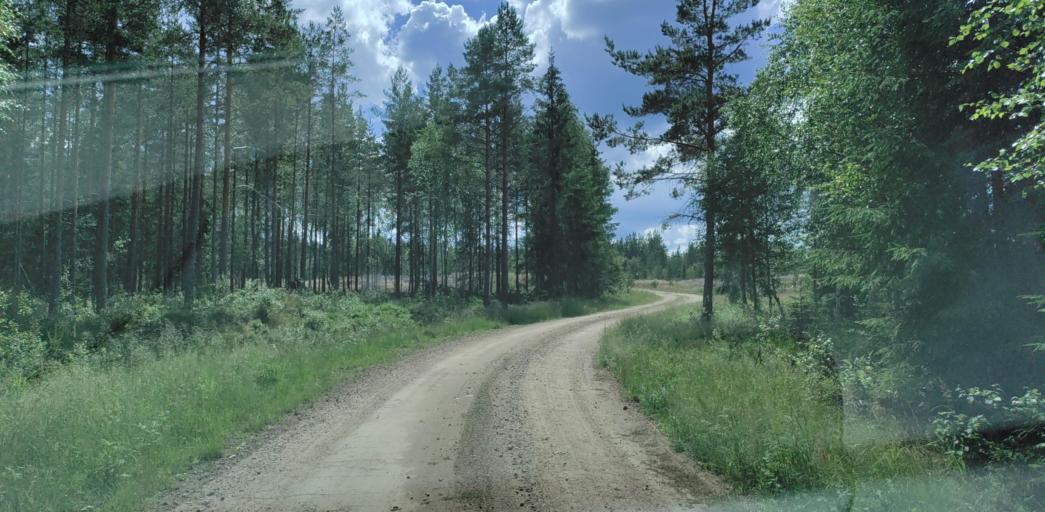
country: SE
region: Vaermland
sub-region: Hagfors Kommun
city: Ekshaerad
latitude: 60.0776
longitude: 13.3463
